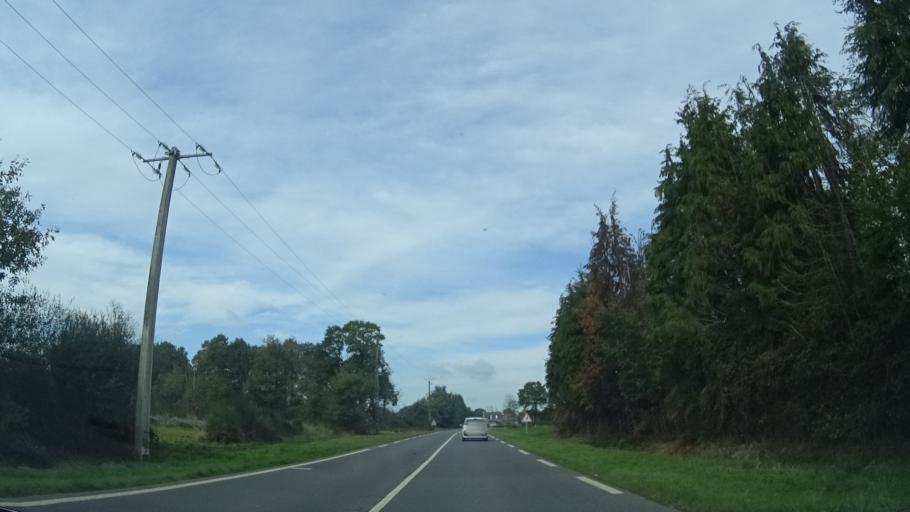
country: FR
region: Brittany
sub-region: Departement d'Ille-et-Vilaine
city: Combourg
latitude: 48.3673
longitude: -1.7635
